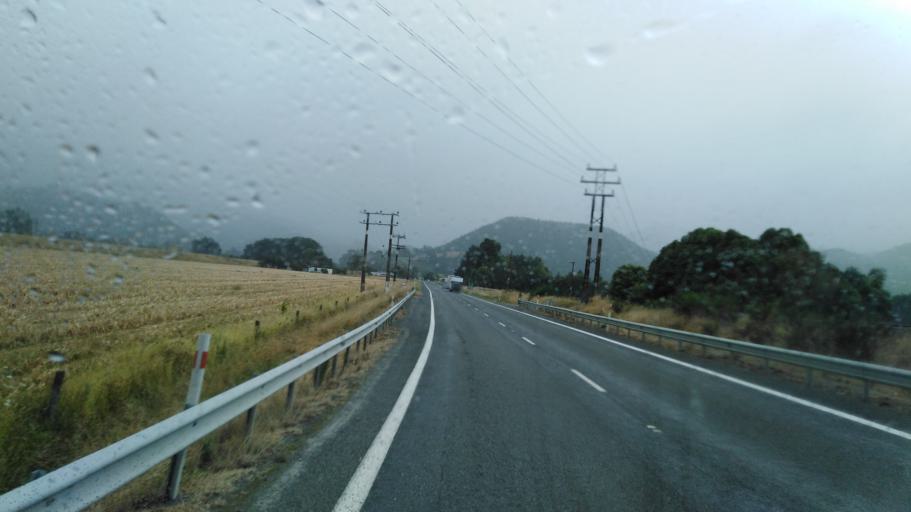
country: NZ
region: Marlborough
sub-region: Marlborough District
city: Blenheim
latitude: -41.4370
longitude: 173.9657
